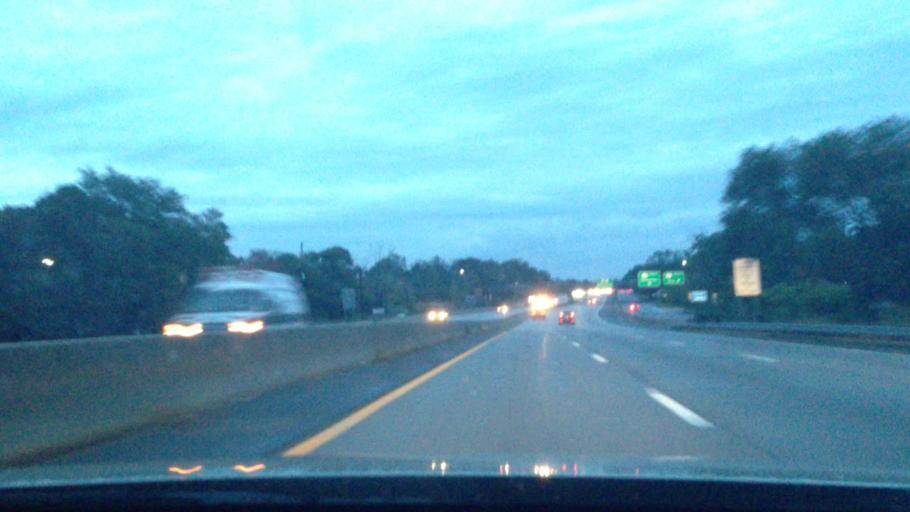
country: US
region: New York
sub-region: Suffolk County
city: Islip
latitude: 40.7417
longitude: -73.2120
